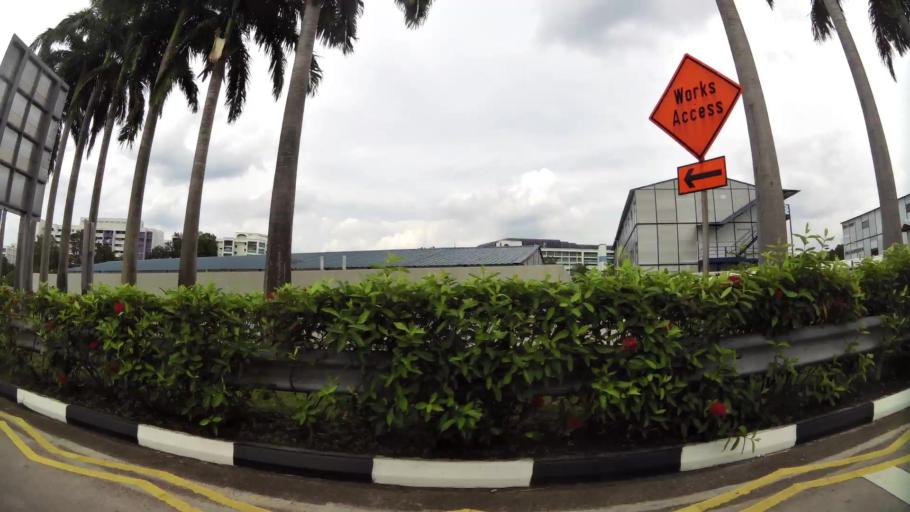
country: MY
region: Johor
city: Johor Bahru
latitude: 1.4383
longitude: 103.7871
